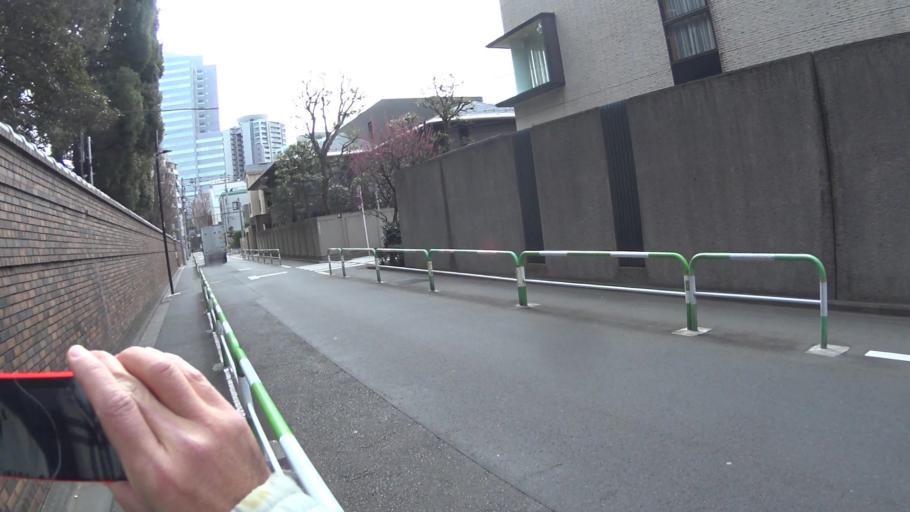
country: JP
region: Tokyo
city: Tokyo
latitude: 35.7318
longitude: 139.7452
